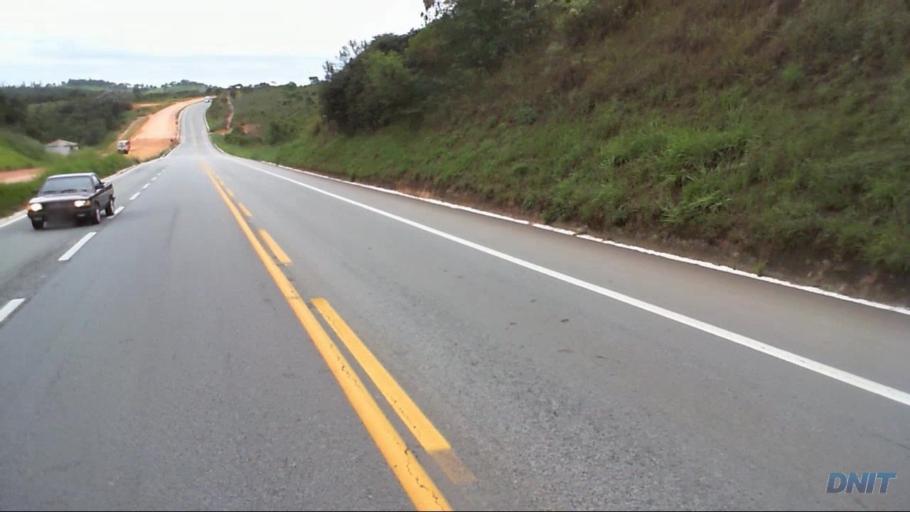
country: BR
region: Minas Gerais
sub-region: Barao De Cocais
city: Barao de Cocais
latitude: -19.7589
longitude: -43.4677
